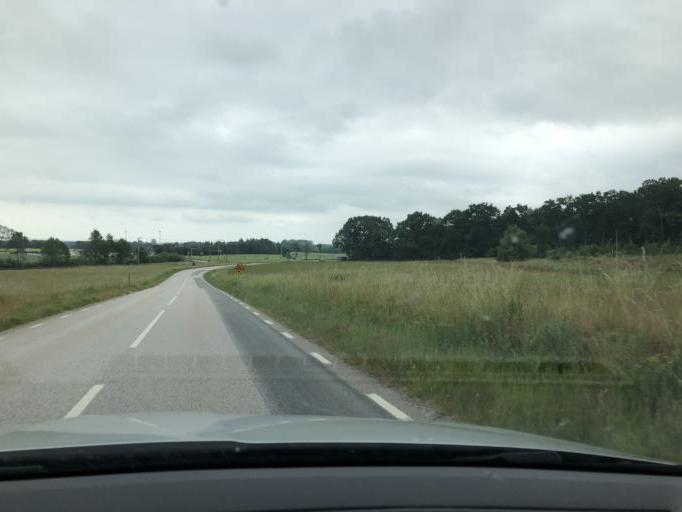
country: SE
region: Blekinge
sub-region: Solvesborgs Kommun
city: Soelvesborg
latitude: 56.0764
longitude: 14.6095
